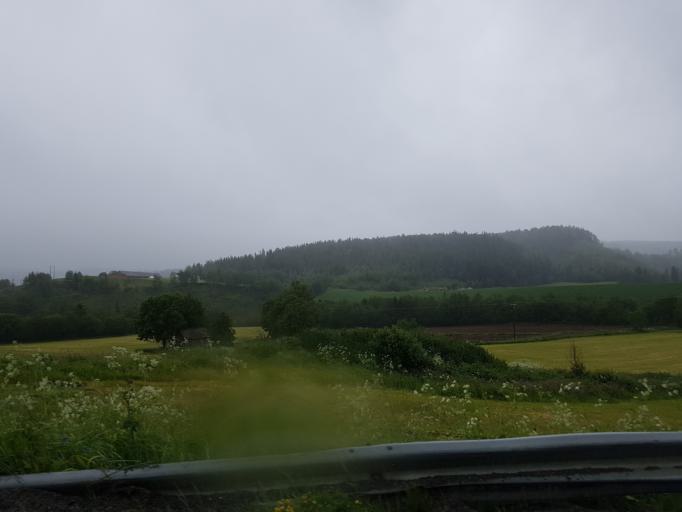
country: NO
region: Sor-Trondelag
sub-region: Selbu
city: Mebonden
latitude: 63.3877
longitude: 11.0736
